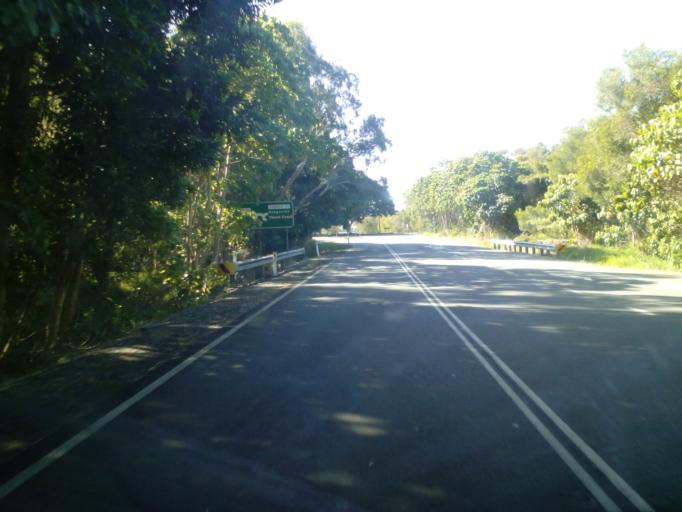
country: AU
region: New South Wales
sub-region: Tweed
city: Kingscliff
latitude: -28.2597
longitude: 153.5703
